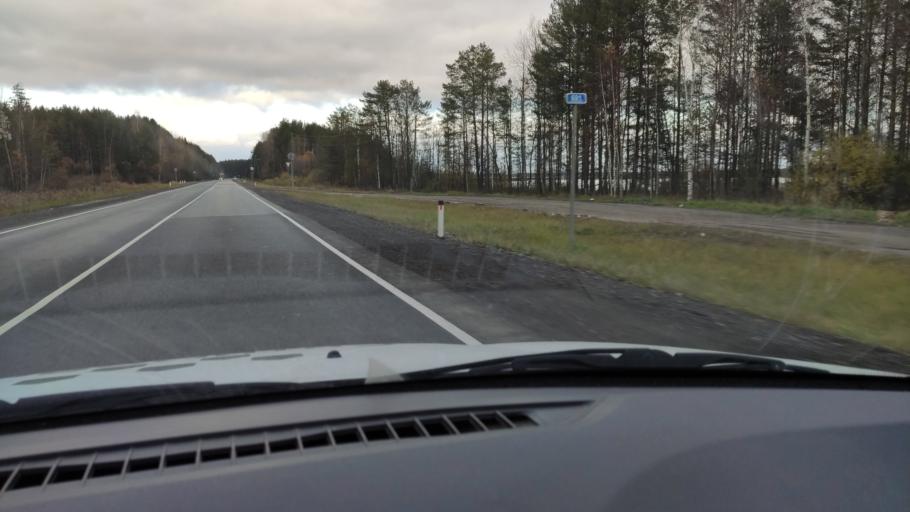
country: RU
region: Kirov
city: Belaya Kholunitsa
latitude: 58.8740
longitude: 50.8600
